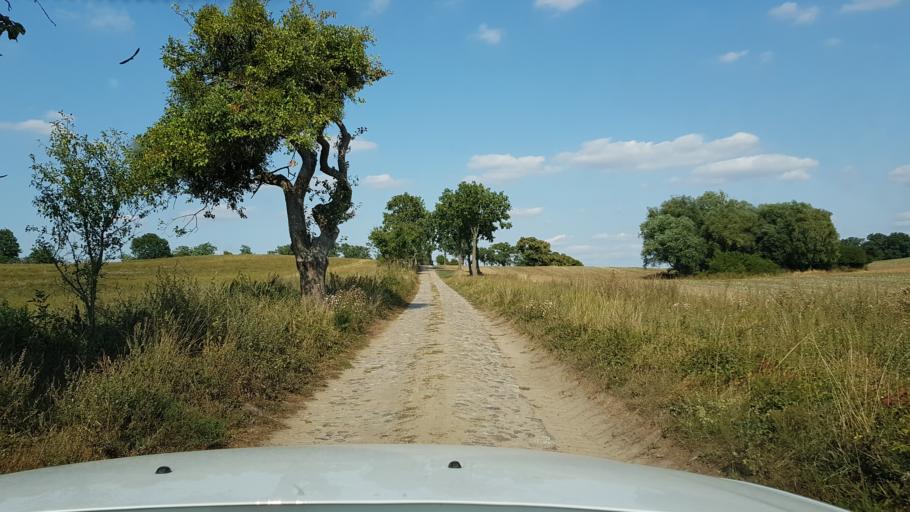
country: PL
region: West Pomeranian Voivodeship
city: Trzcinsko Zdroj
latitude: 52.9034
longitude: 14.5745
